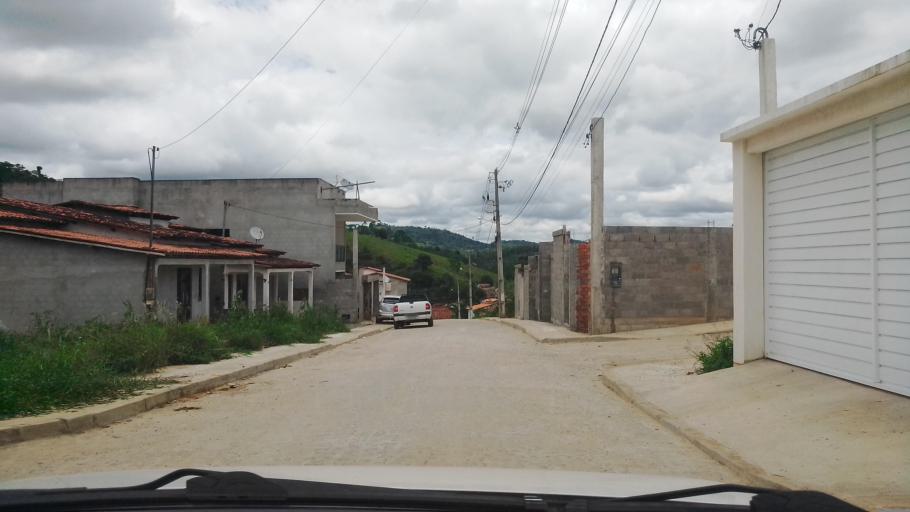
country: BR
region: Bahia
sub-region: Mutuipe
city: Mutuipe
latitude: -13.2556
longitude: -39.5665
